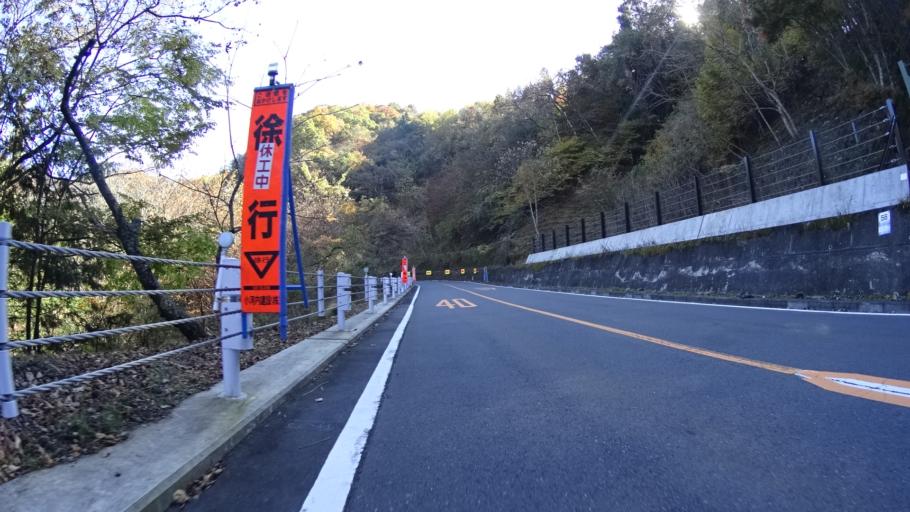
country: JP
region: Yamanashi
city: Uenohara
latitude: 35.7561
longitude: 139.0295
